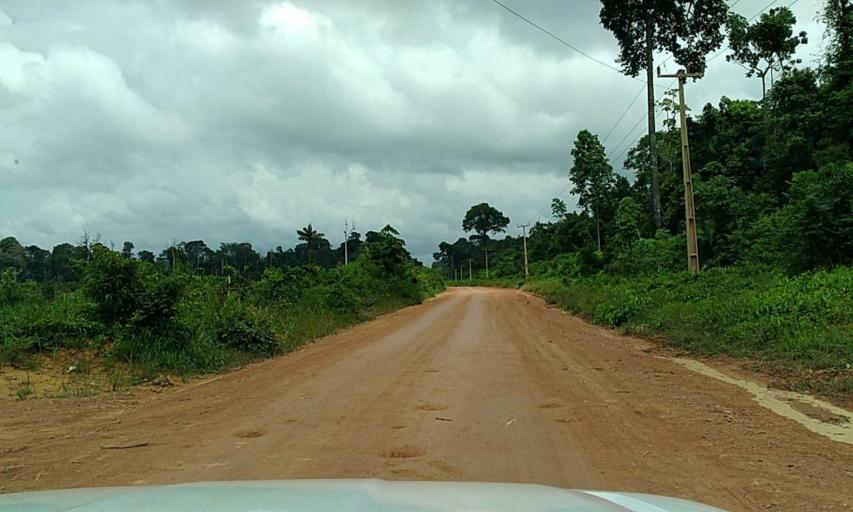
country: BR
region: Para
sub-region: Senador Jose Porfirio
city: Senador Jose Porfirio
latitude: -2.6826
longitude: -51.8304
